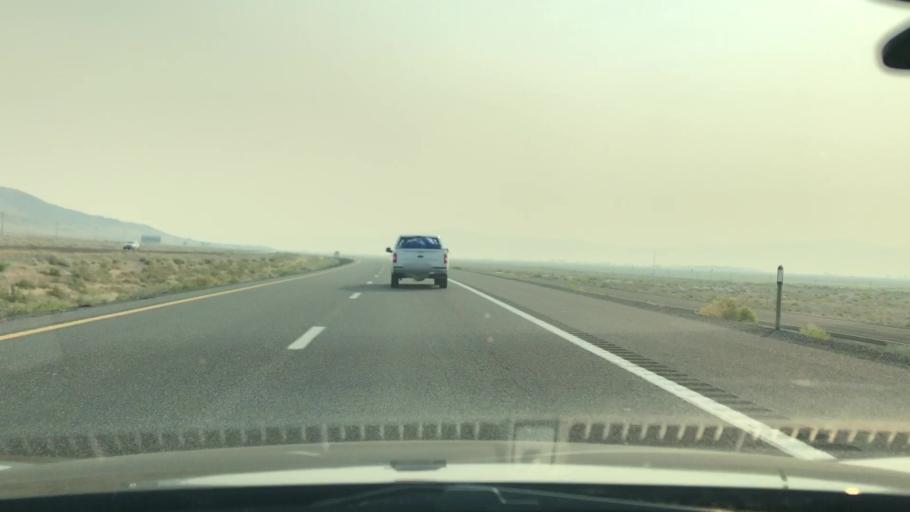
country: US
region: Nevada
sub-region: Pershing County
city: Lovelock
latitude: 40.1075
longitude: -118.5575
